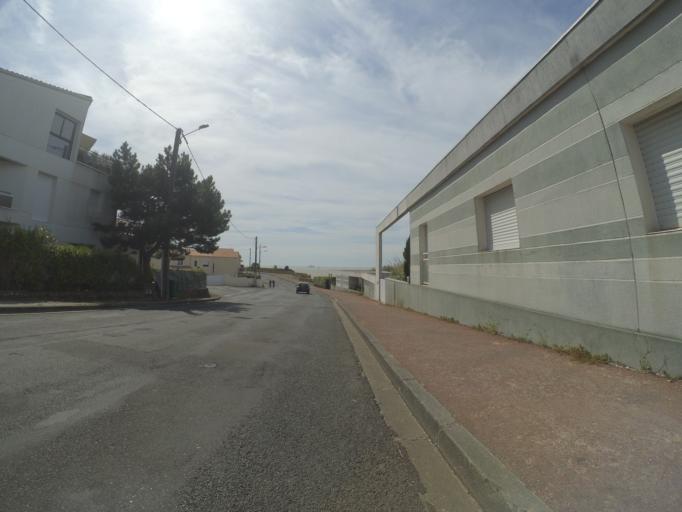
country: FR
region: Poitou-Charentes
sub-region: Departement de la Charente-Maritime
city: Saint-Georges-de-Didonne
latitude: 45.6050
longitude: -1.0106
